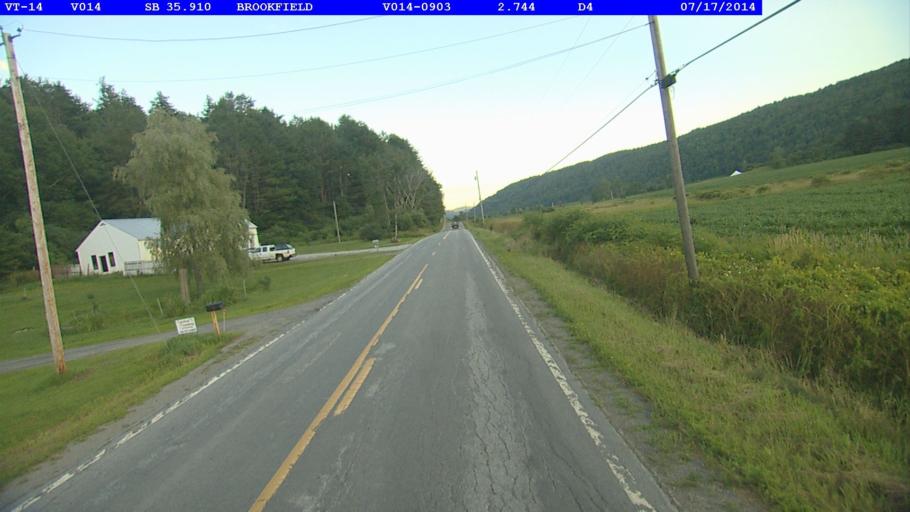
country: US
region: Vermont
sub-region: Orange County
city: Williamstown
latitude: 44.0165
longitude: -72.5696
